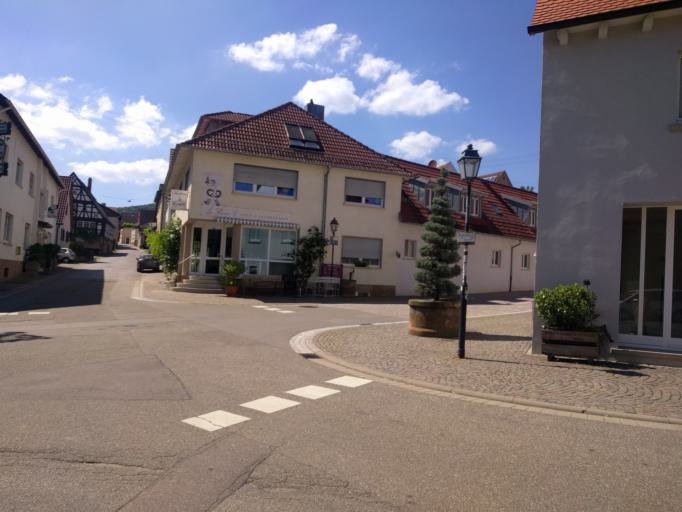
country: DE
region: Rheinland-Pfalz
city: Schweigen-Rechtenbach
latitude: 49.0509
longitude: 7.9522
